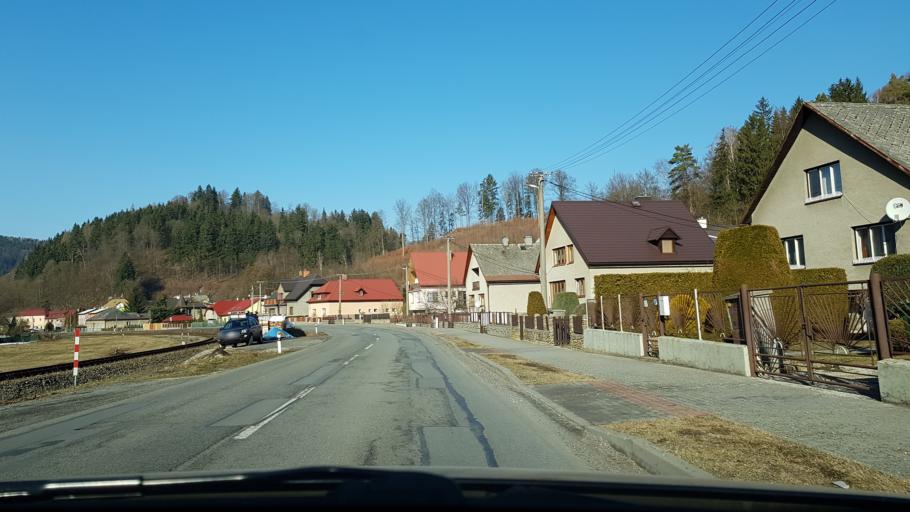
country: CZ
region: Olomoucky
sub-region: Okres Sumperk
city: Hanusovice
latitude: 50.0799
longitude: 16.9431
